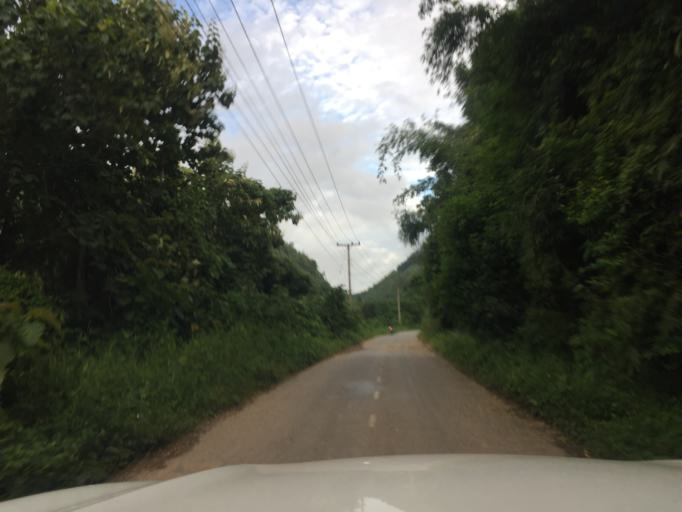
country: LA
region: Phongsali
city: Khoa
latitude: 21.1034
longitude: 102.3036
